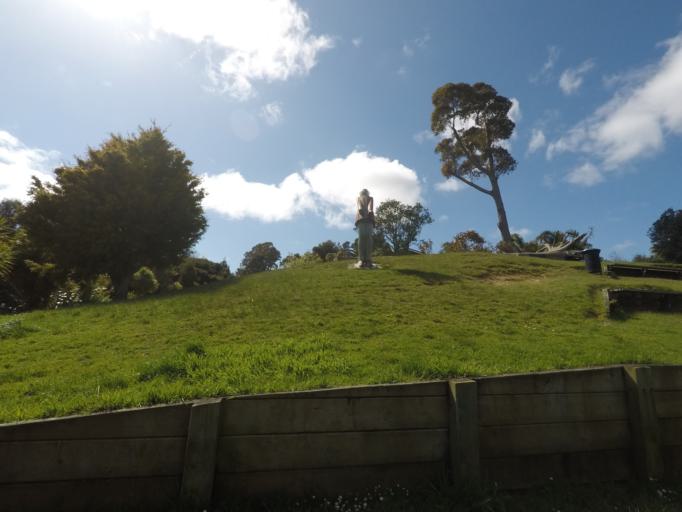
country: NZ
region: Auckland
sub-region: Auckland
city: Auckland
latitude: -36.8597
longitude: 174.7391
